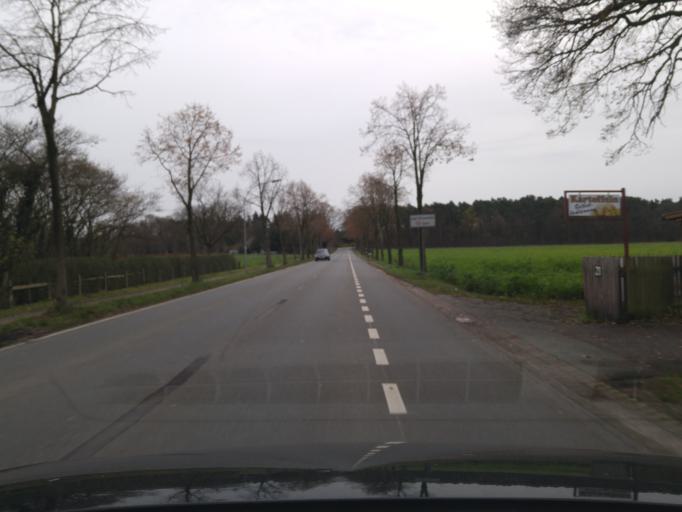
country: DE
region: Lower Saxony
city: Winsen
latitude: 52.7343
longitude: 9.9271
